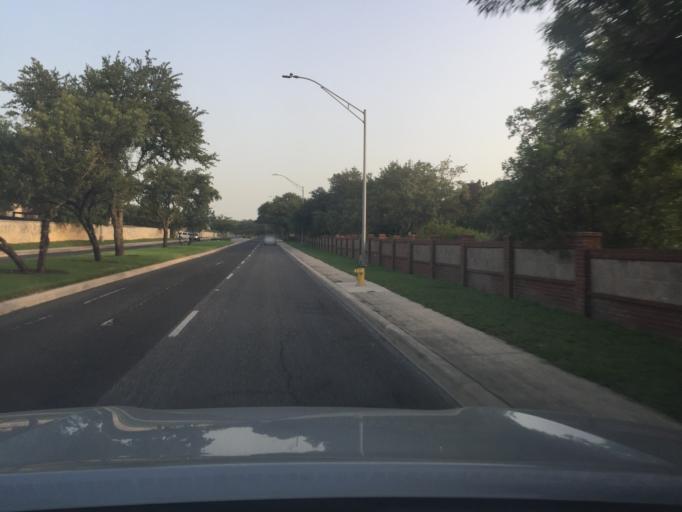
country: US
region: Texas
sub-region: Bexar County
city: Hollywood Park
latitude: 29.6504
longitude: -98.4950
